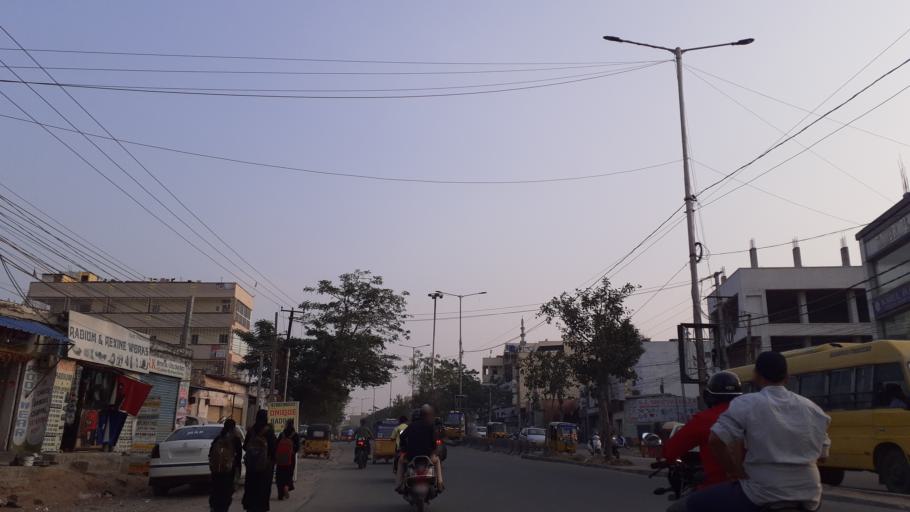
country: IN
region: Telangana
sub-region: Rangareddi
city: Kukatpalli
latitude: 17.4794
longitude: 78.3613
